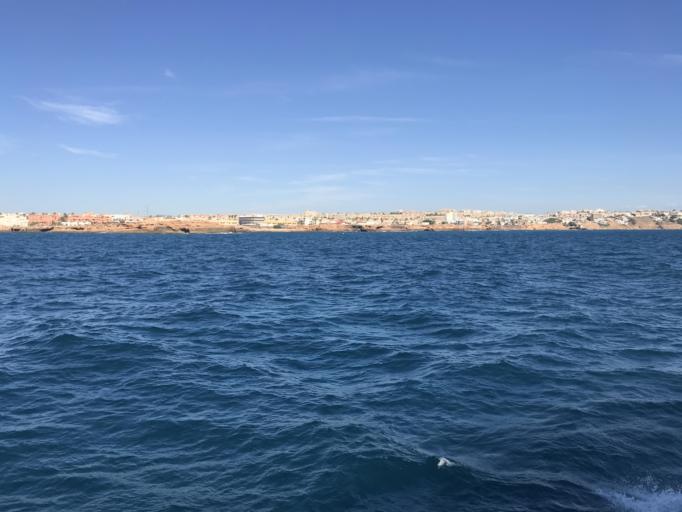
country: ES
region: Valencia
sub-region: Provincia de Alicante
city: Torrevieja
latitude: 37.9828
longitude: -0.6515
